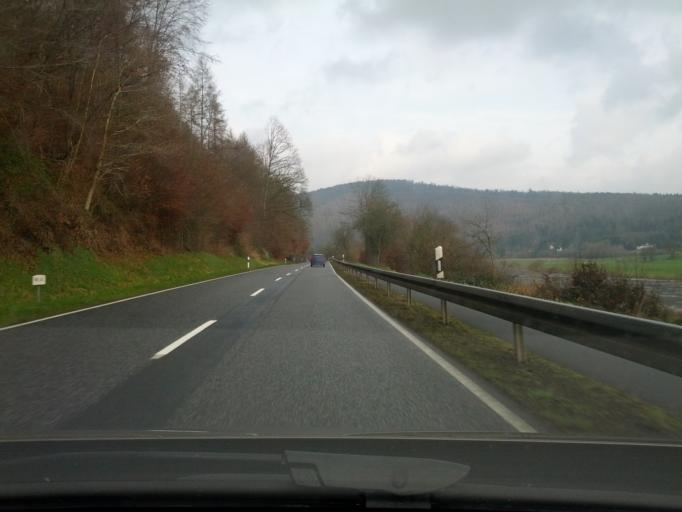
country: DE
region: Lower Saxony
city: Bad Karlshafen
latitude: 51.6434
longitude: 9.4918
